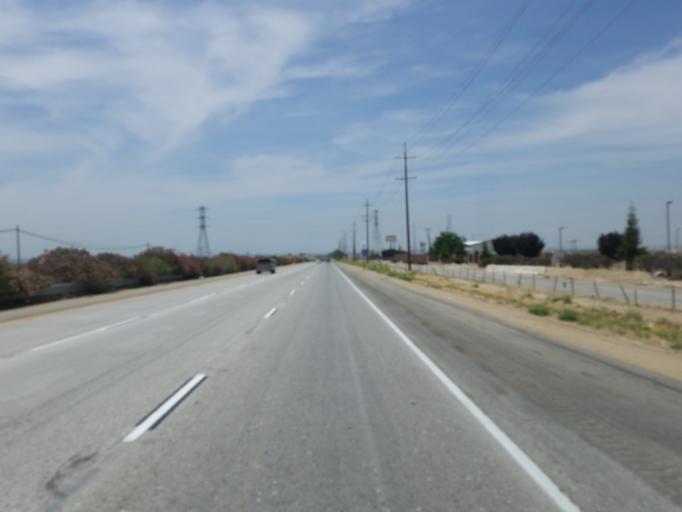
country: US
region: California
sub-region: Kern County
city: Weedpatch
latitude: 35.0835
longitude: -118.9758
